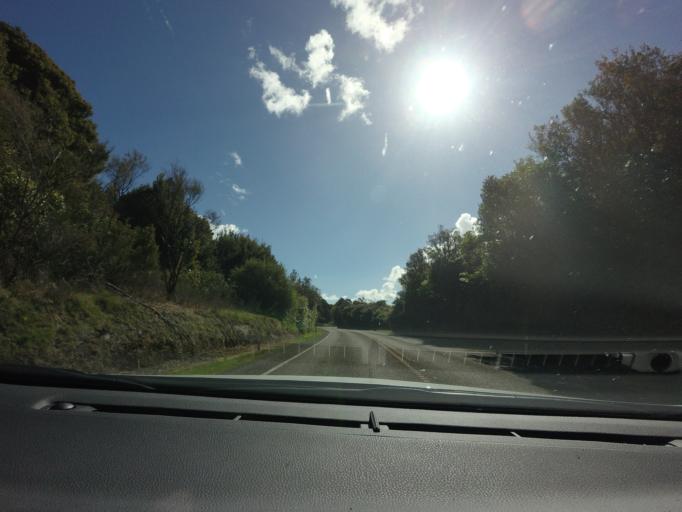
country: NZ
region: Waikato
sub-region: South Waikato District
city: Tokoroa
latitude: -38.0341
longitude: 176.0118
